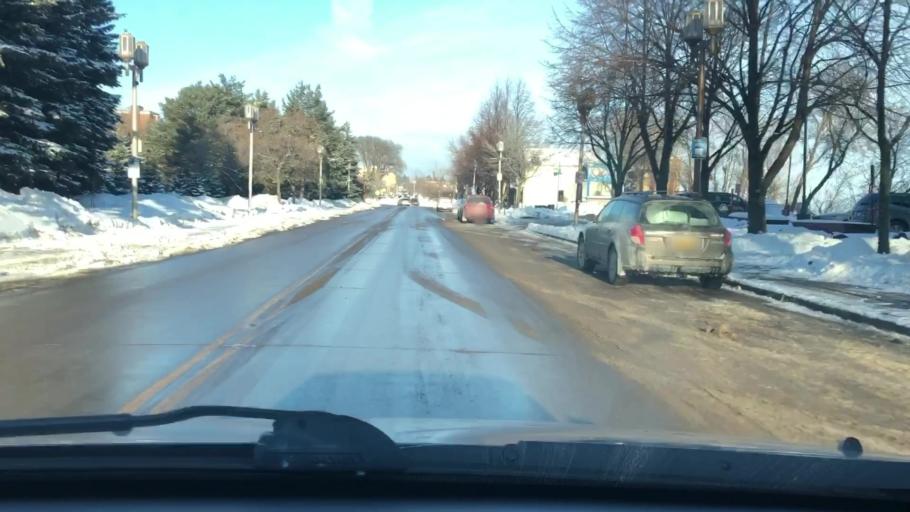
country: US
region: Minnesota
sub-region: Saint Louis County
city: Duluth
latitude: 46.7928
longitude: -92.0905
